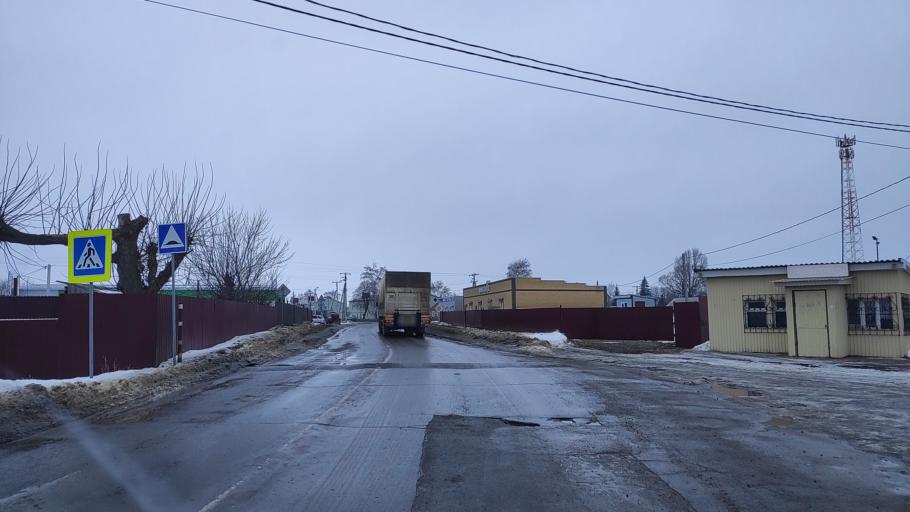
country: RU
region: Tambov
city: Novopokrovka
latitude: 51.9916
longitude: 41.1568
